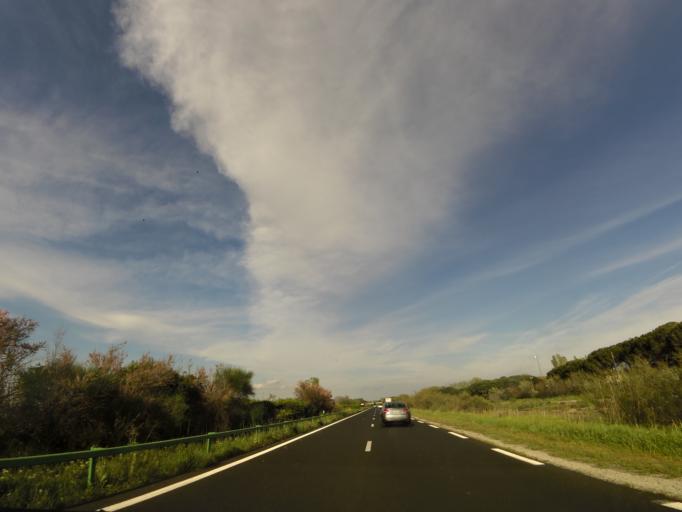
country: FR
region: Languedoc-Roussillon
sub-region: Departement de l'Herault
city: La Grande-Motte
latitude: 43.5686
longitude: 4.0692
